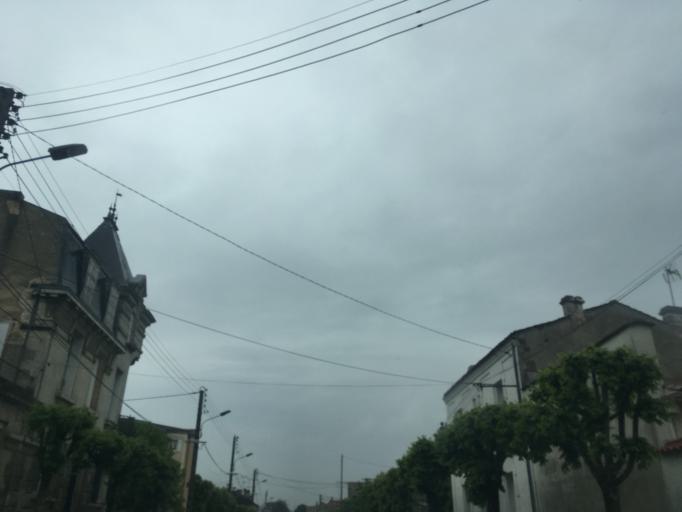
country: FR
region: Poitou-Charentes
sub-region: Departement de la Charente
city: Cognac
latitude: 45.6886
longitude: -0.3243
